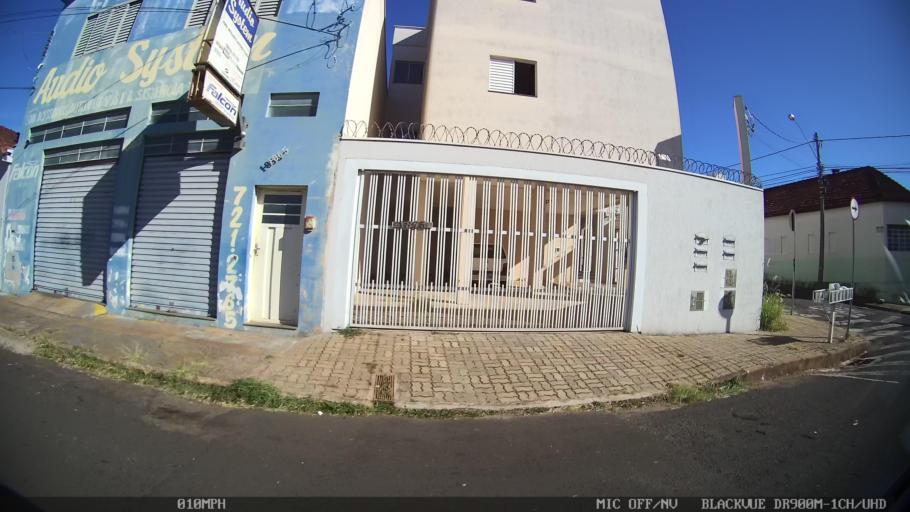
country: BR
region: Sao Paulo
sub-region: Franca
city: Franca
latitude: -20.5353
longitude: -47.4088
